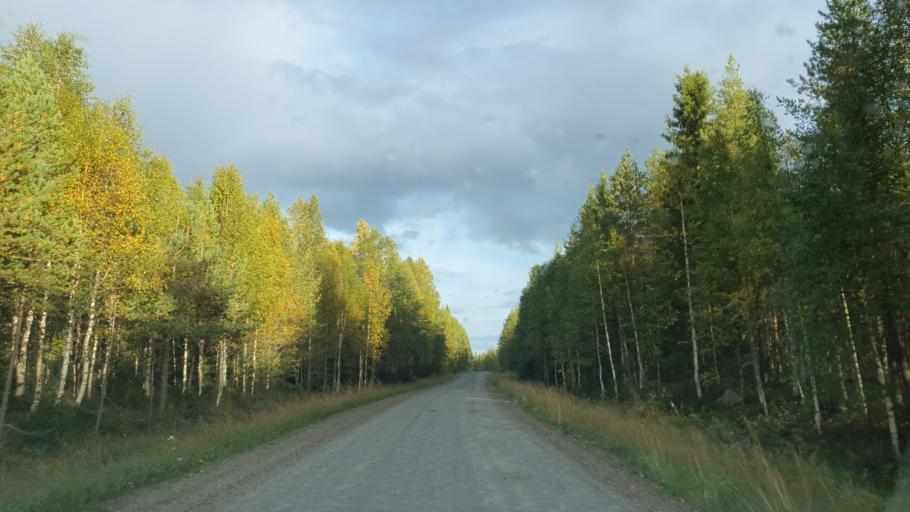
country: FI
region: Kainuu
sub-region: Kehys-Kainuu
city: Kuhmo
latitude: 64.4244
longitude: 29.3484
